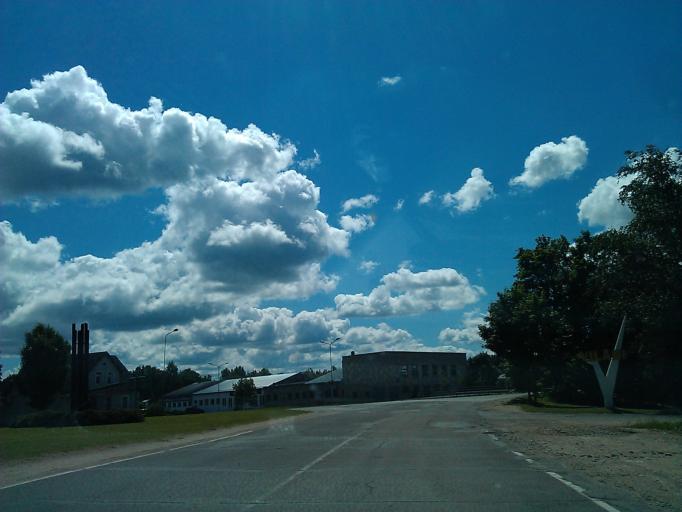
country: LV
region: Vilanu
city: Vilani
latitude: 56.5667
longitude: 26.9284
